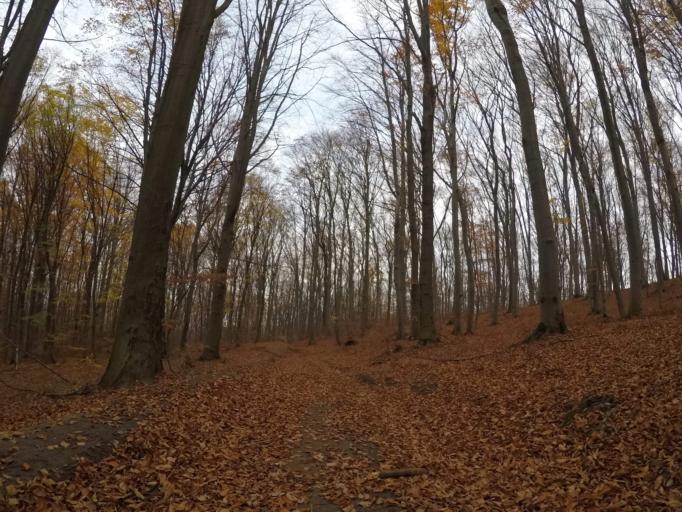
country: SK
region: Presovsky
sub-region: Okres Presov
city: Presov
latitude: 48.9377
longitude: 21.1274
